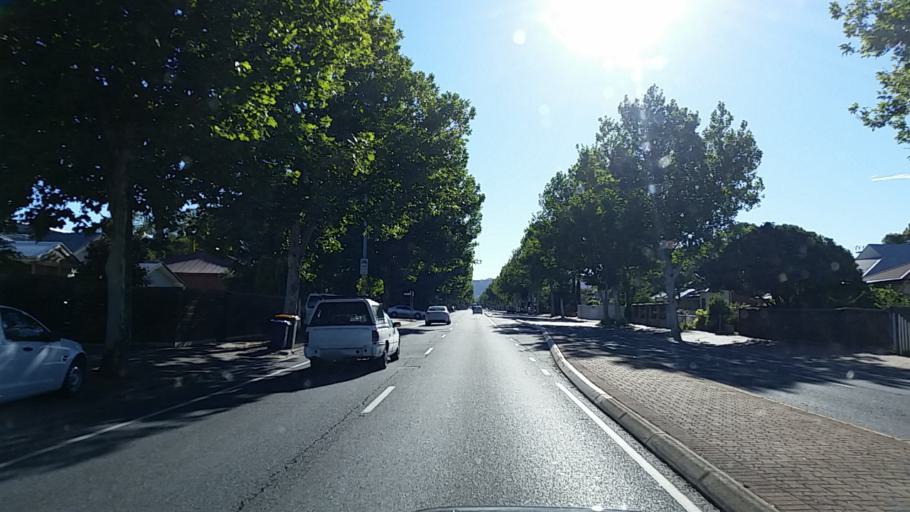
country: AU
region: South Australia
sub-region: Mitcham
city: Clarence Gardens
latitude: -34.9670
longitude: 138.5766
